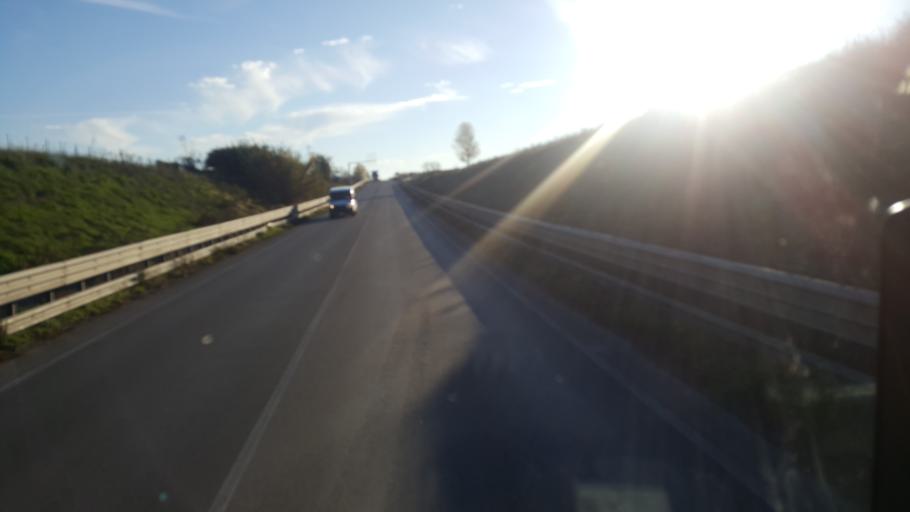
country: IT
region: Emilia-Romagna
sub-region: Provincia di Parma
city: Ponte Taro
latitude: 44.8334
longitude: 10.2235
